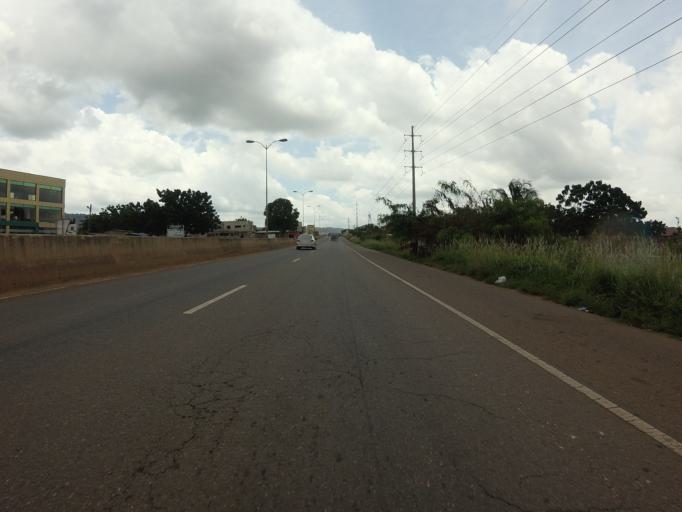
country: GH
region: Eastern
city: Aburi
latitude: 5.7580
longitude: -0.1789
